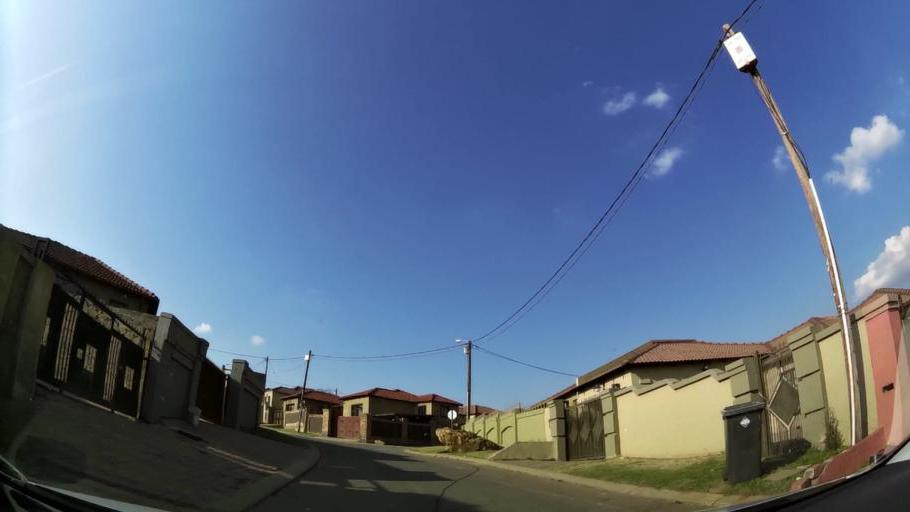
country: ZA
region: Gauteng
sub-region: Ekurhuleni Metropolitan Municipality
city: Tembisa
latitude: -25.9546
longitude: 28.2112
